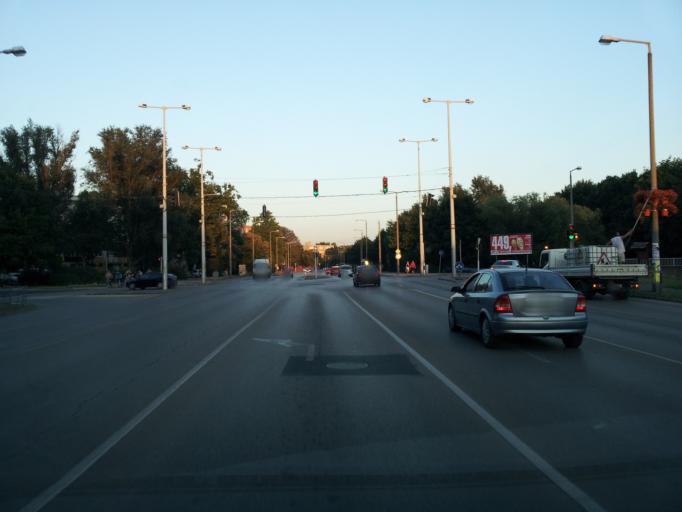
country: HU
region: Komarom-Esztergom
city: Tatabanya
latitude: 47.5762
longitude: 18.4036
